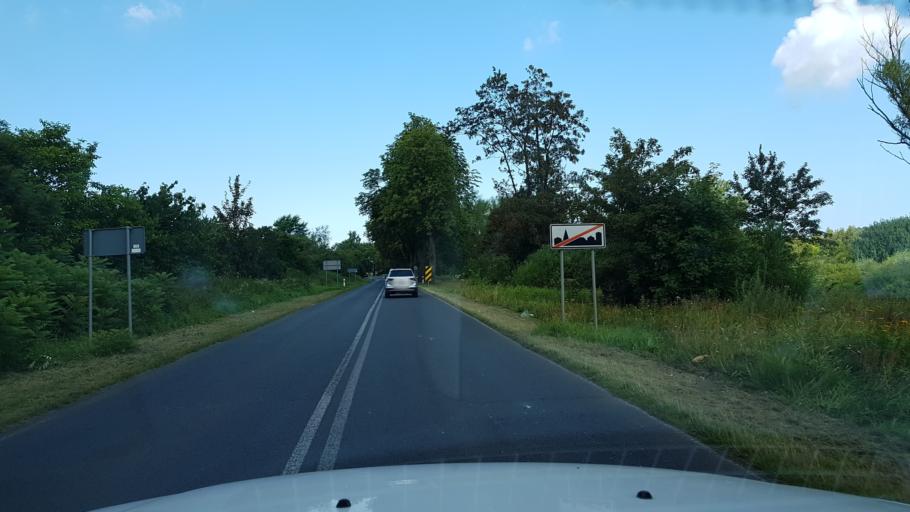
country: PL
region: West Pomeranian Voivodeship
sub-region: Powiat gryficki
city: Trzebiatow
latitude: 54.0663
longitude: 15.2513
